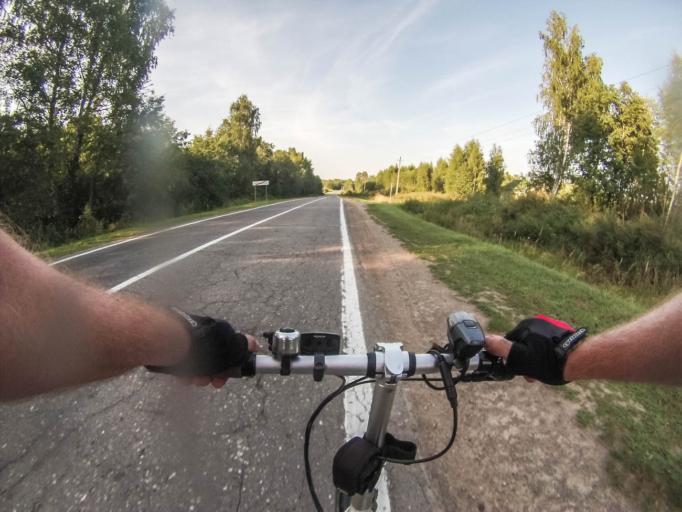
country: RU
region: Jaroslavl
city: Myshkin
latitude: 57.7507
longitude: 38.4371
